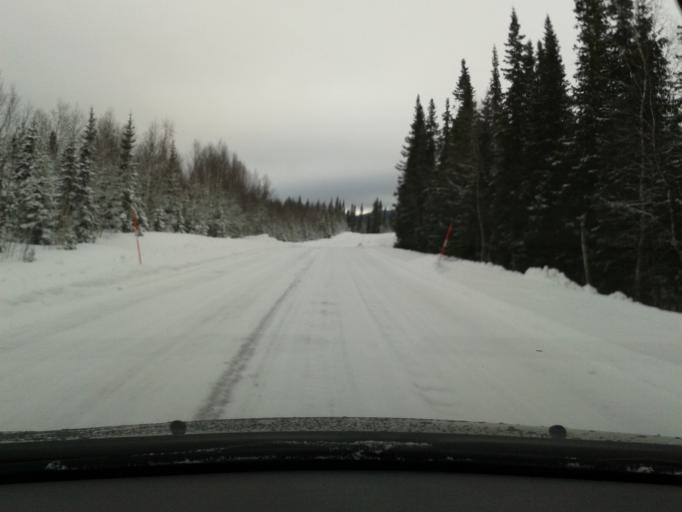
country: SE
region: Vaesterbotten
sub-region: Vilhelmina Kommun
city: Sjoberg
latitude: 65.2301
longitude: 15.8764
